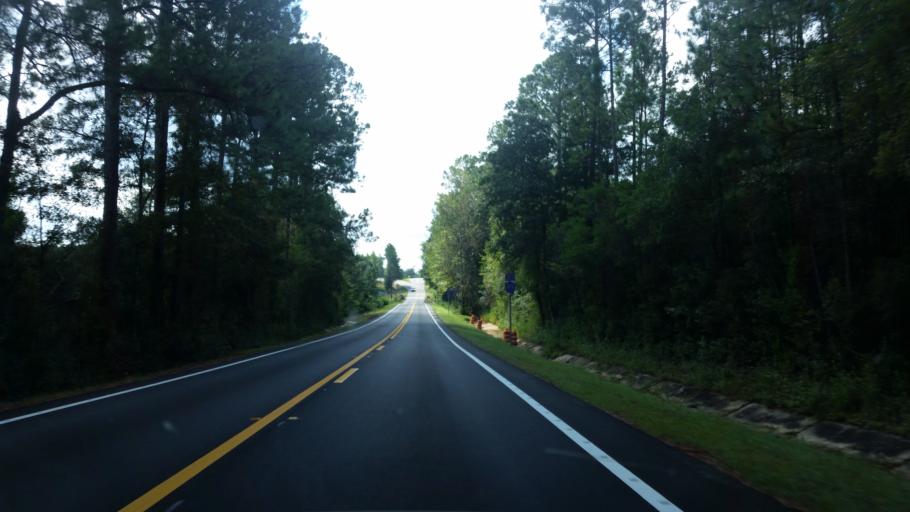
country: US
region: Florida
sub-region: Escambia County
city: Molino
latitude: 30.6879
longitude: -87.4041
